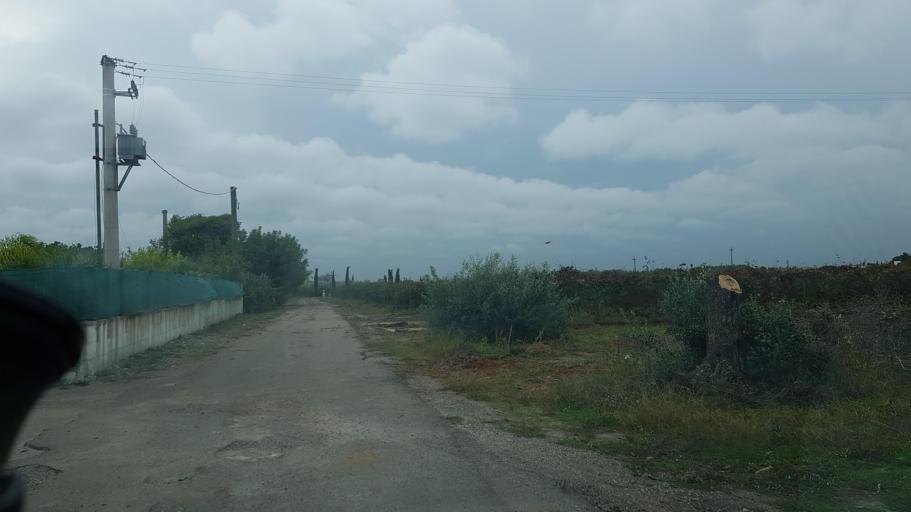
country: IT
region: Apulia
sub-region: Provincia di Brindisi
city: San Donaci
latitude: 40.4514
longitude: 17.9361
